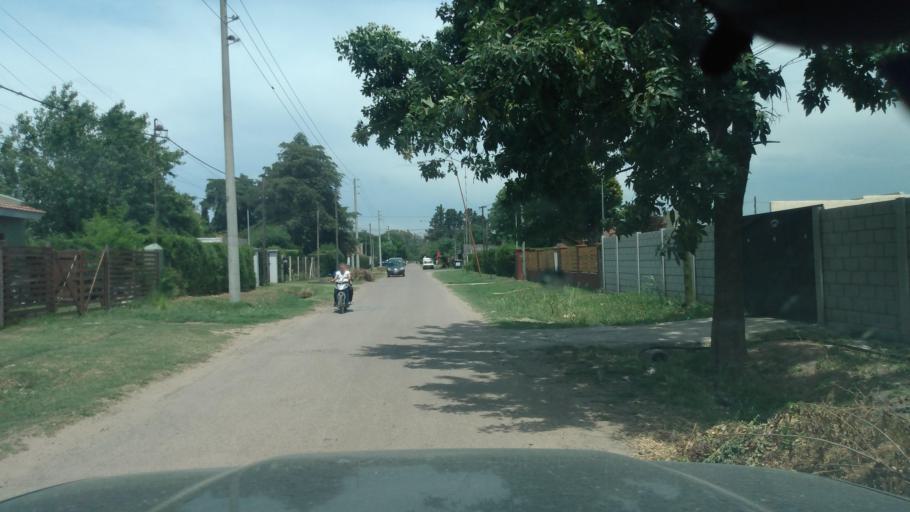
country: AR
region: Buenos Aires
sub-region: Partido de Lujan
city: Lujan
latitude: -34.5446
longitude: -59.1409
